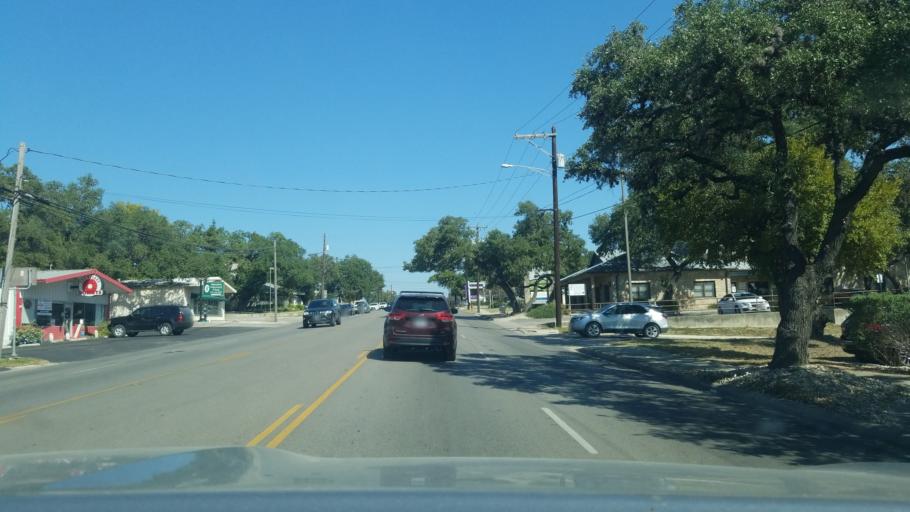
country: US
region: Texas
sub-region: Kendall County
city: Boerne
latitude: 29.7813
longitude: -98.7290
